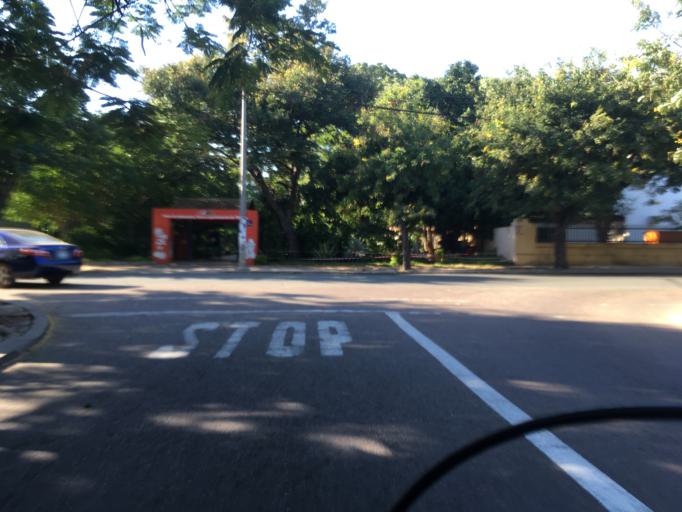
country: MZ
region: Maputo City
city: Maputo
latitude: -25.9687
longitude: 32.5927
